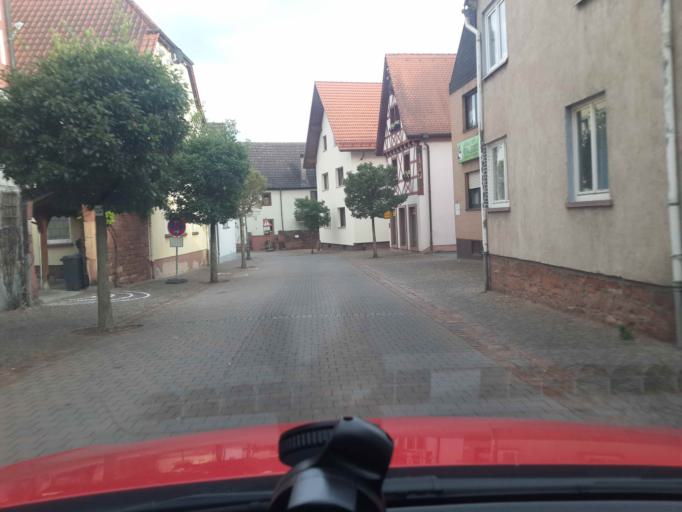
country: DE
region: Bavaria
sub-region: Regierungsbezirk Unterfranken
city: Grossheubach
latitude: 49.7266
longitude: 9.2202
